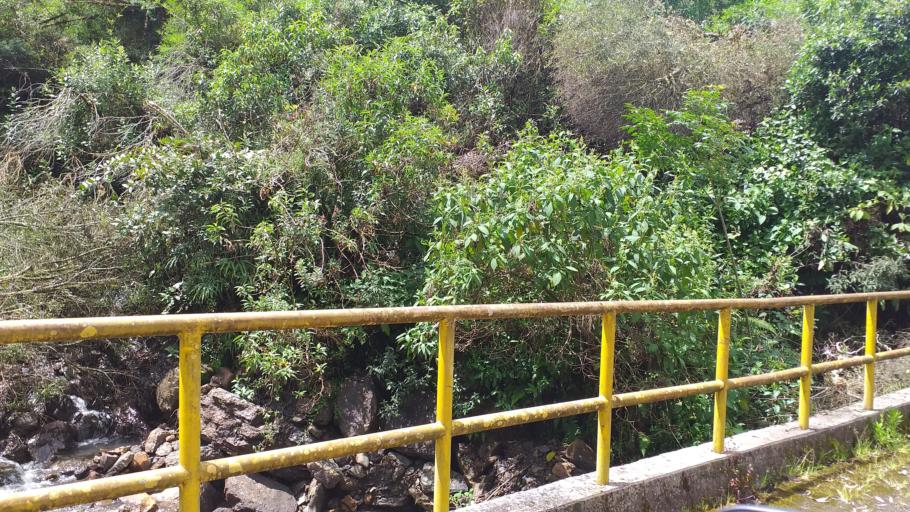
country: CO
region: Cundinamarca
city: Tenza
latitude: 5.1279
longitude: -73.4572
